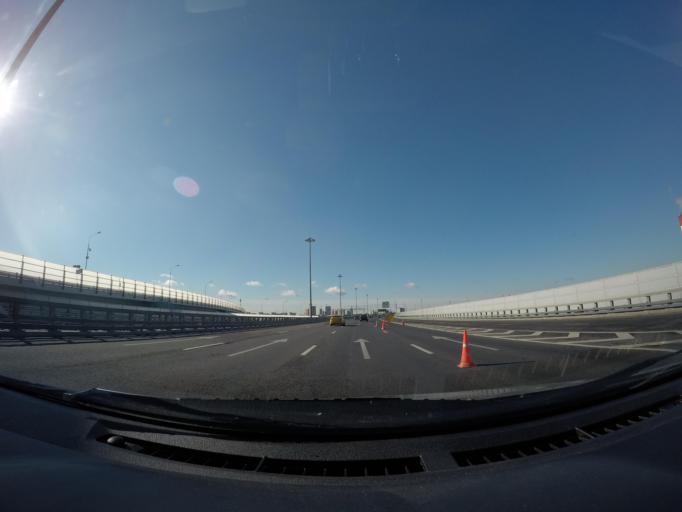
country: RU
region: Moscow
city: Ryazanskiy
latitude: 55.7534
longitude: 37.7463
